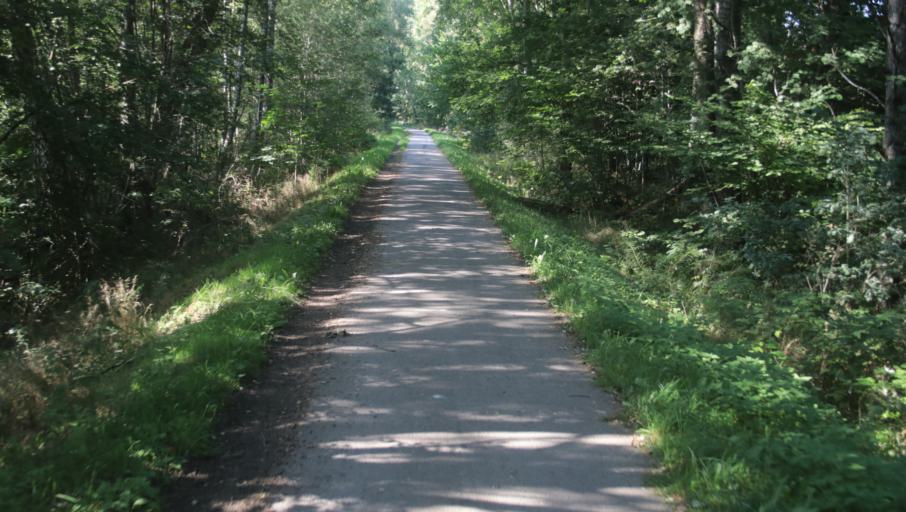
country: SE
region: Blekinge
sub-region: Karlshamns Kommun
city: Svangsta
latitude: 56.2399
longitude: 14.8018
